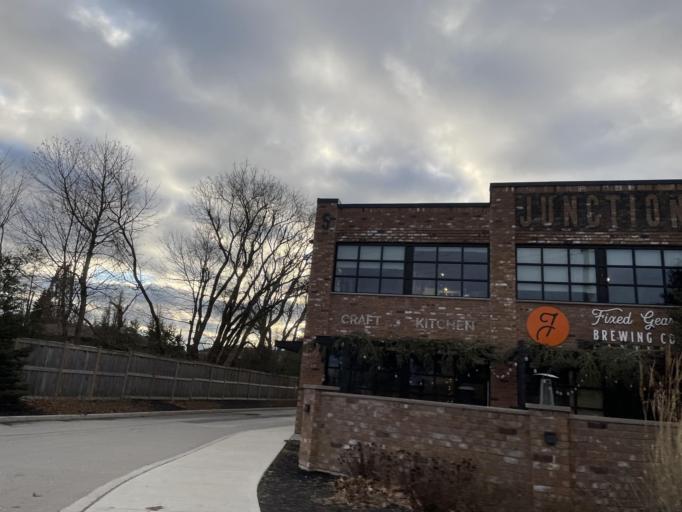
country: CA
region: Ontario
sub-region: Wellington County
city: Guelph
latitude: 43.5376
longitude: -80.2582
